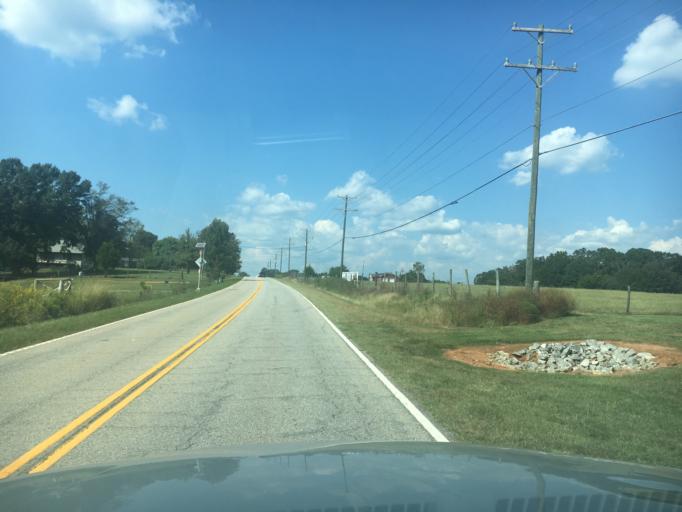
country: US
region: South Carolina
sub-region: Anderson County
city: Pendleton
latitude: 34.5678
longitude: -82.8072
